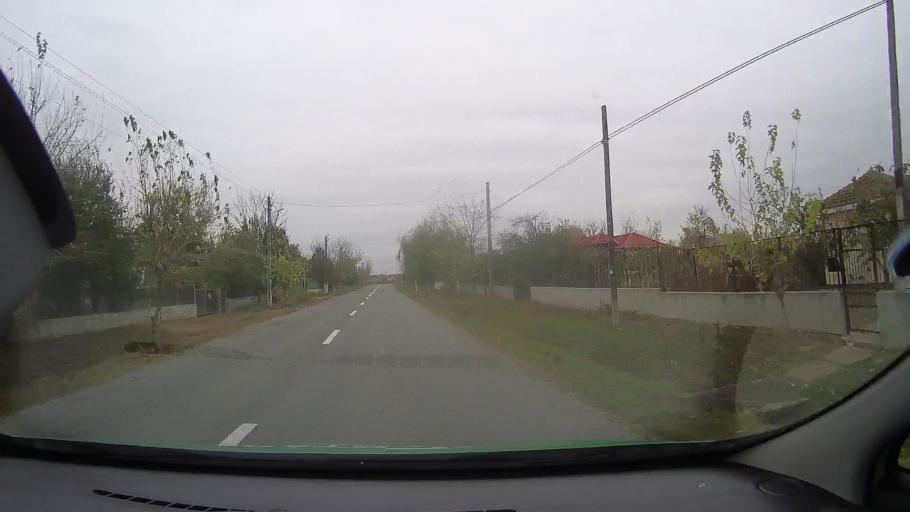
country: RO
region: Constanta
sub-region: Comuna Crucea
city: Crucea
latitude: 44.4492
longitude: 28.2415
